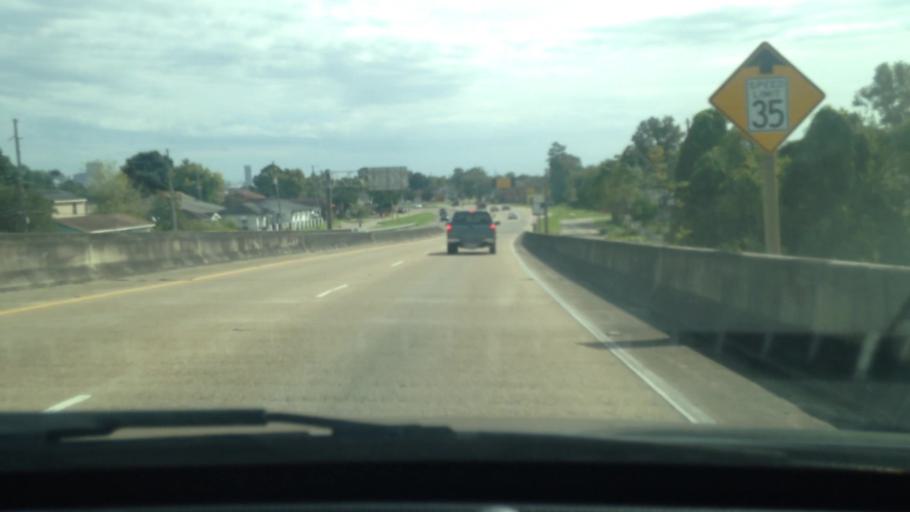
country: US
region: Louisiana
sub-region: Jefferson Parish
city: Jefferson
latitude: 29.9671
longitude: -90.1281
